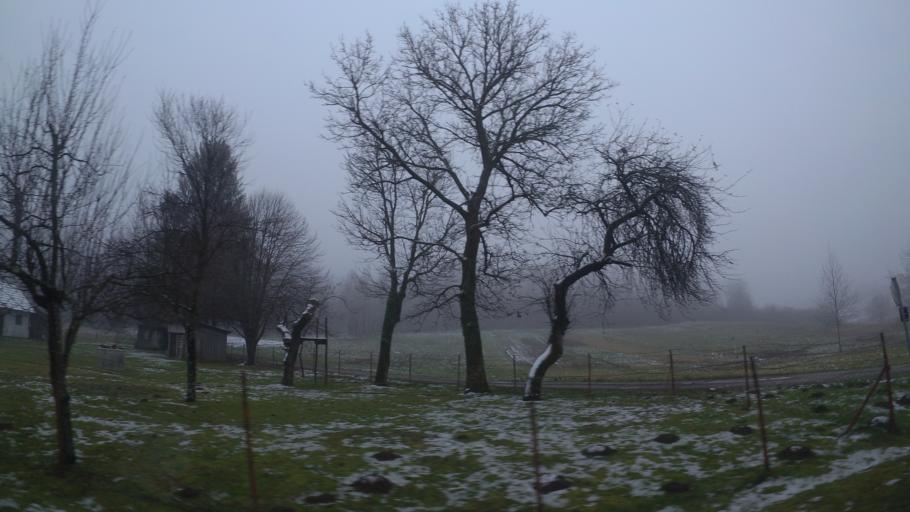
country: HR
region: Sisacko-Moslavacka
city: Glina
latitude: 45.3053
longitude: 16.0035
